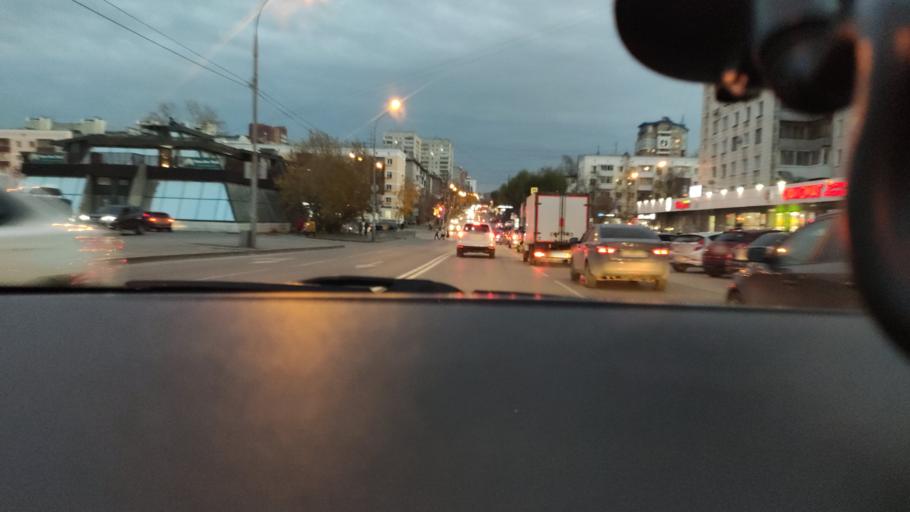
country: RU
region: Perm
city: Perm
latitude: 58.0077
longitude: 56.2122
